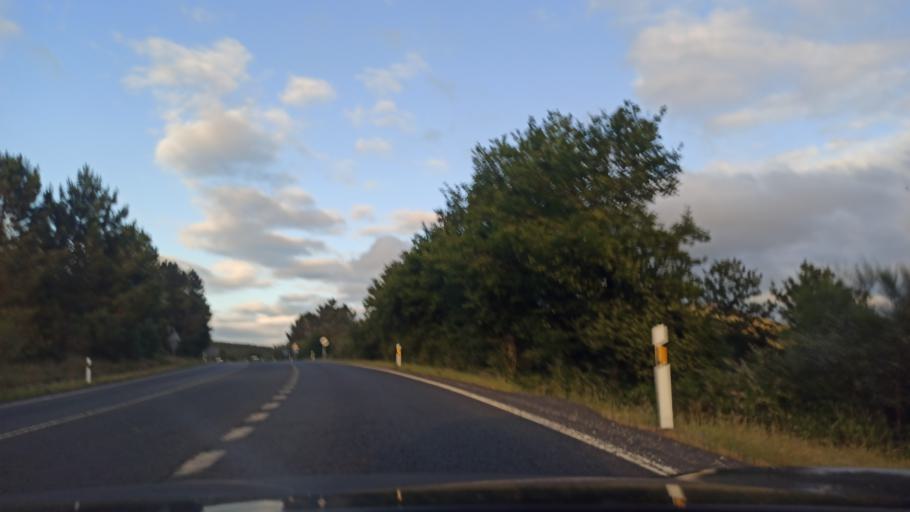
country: ES
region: Galicia
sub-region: Provincia de Pontevedra
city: Rodeiro
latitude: 42.7685
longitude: -7.9784
